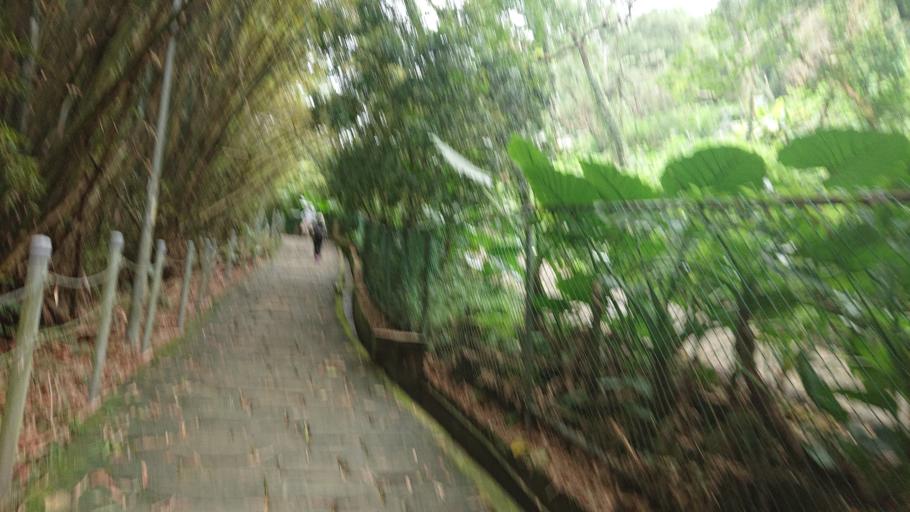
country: TW
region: Taipei
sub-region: Taipei
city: Banqiao
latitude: 24.9537
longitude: 121.4443
